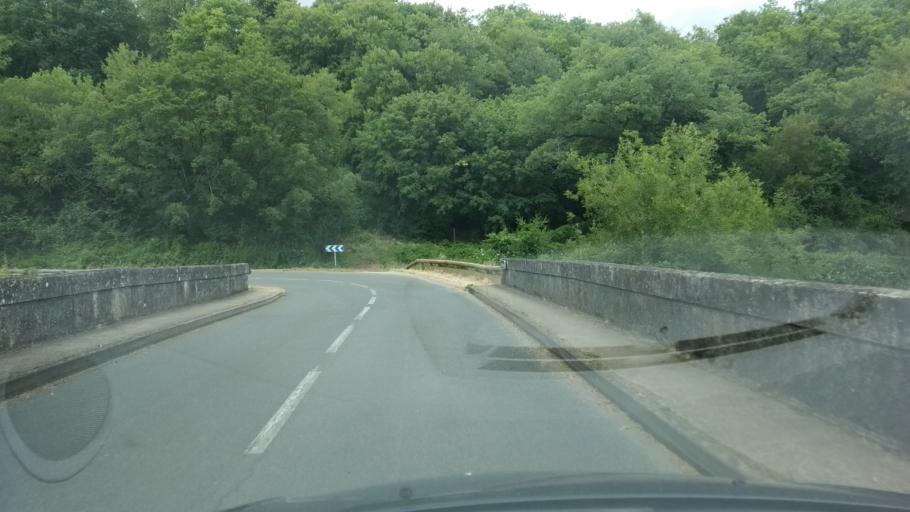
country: FR
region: Poitou-Charentes
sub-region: Departement de la Vienne
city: Vouneuil-sous-Biard
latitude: 46.5798
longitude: 0.2735
